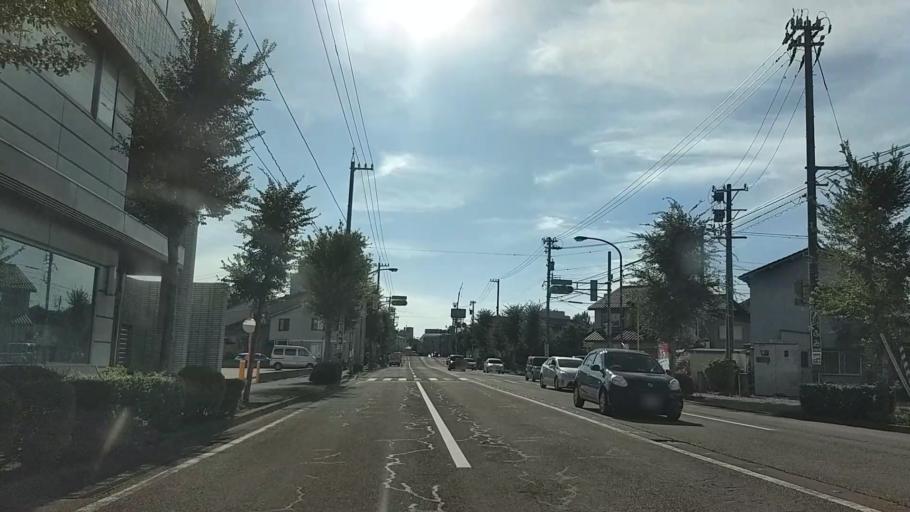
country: JP
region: Ishikawa
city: Kanazawa-shi
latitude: 36.5778
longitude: 136.6636
